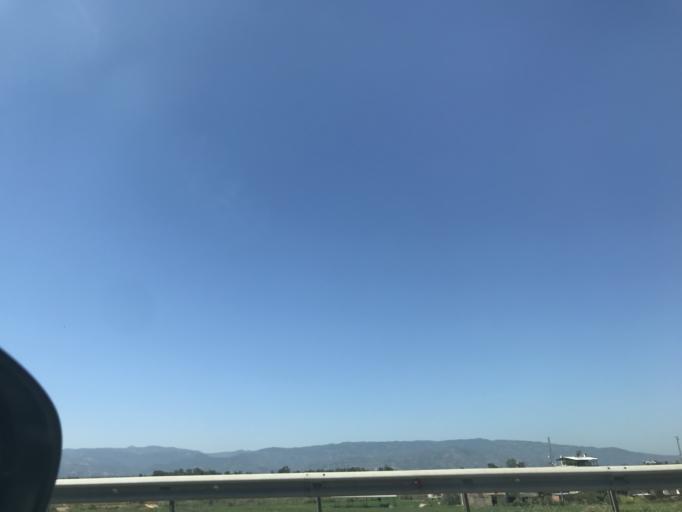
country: TR
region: Aydin
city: Aydin
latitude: 37.8230
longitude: 27.8175
